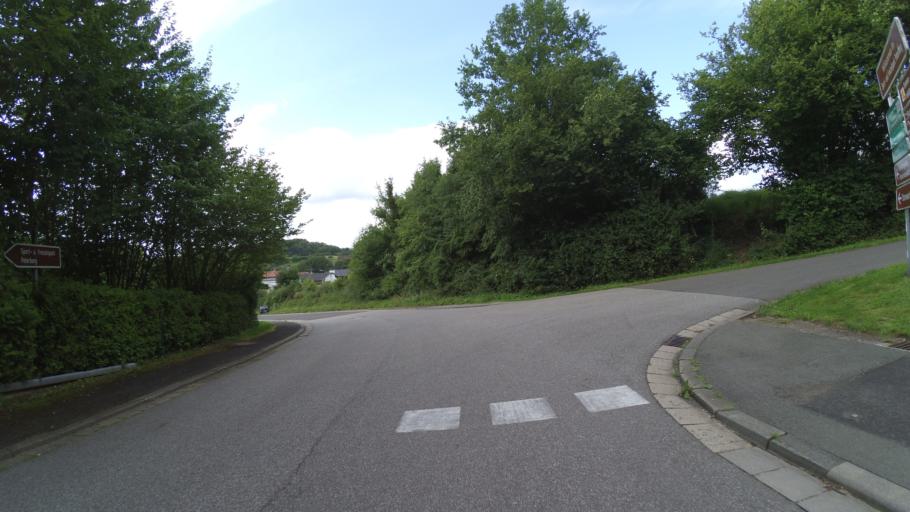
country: DE
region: Rheinland-Pfalz
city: Neuhutten
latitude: 49.5810
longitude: 7.0025
